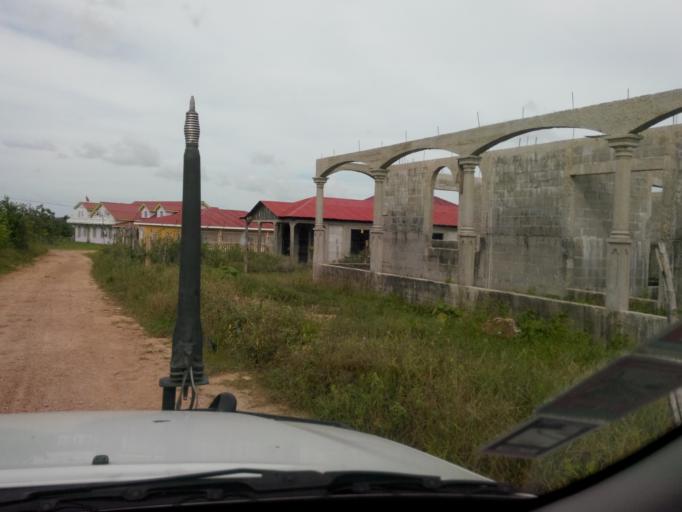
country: NI
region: Atlantico Sur
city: Bluefields
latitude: 12.0308
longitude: -83.7650
